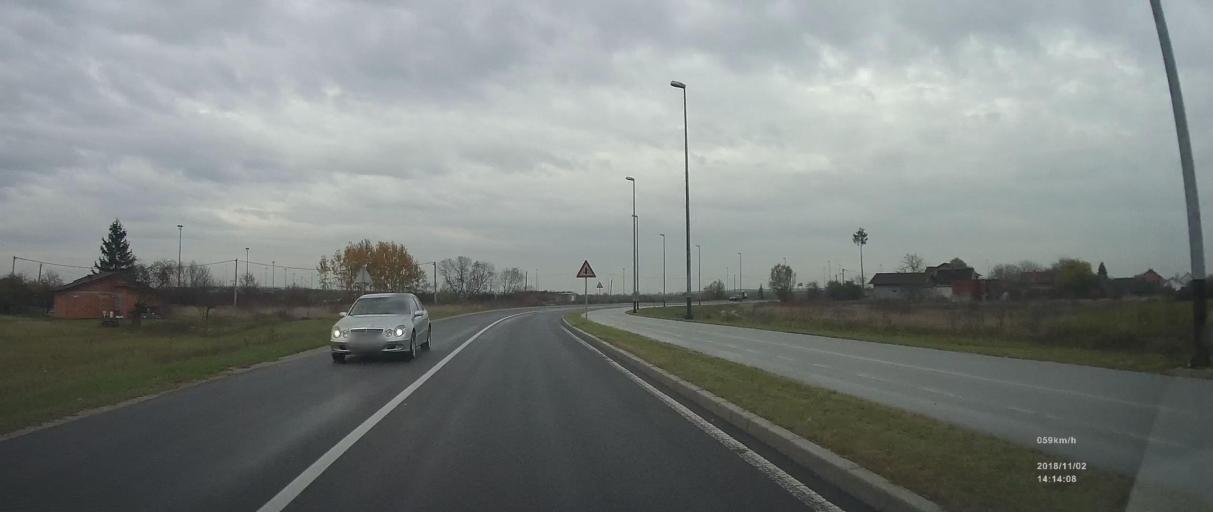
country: HR
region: Zagrebacka
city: Gradici
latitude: 45.6935
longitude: 16.0609
